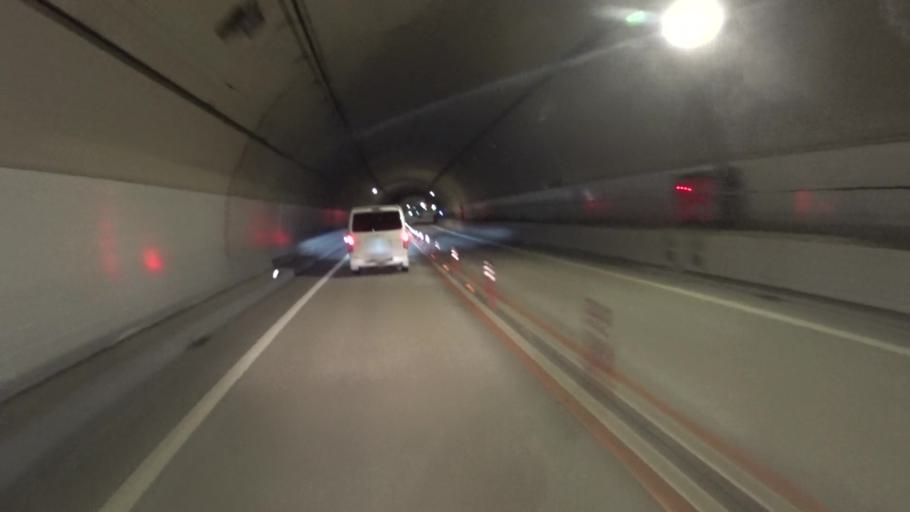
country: JP
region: Kyoto
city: Miyazu
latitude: 35.5301
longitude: 135.1700
